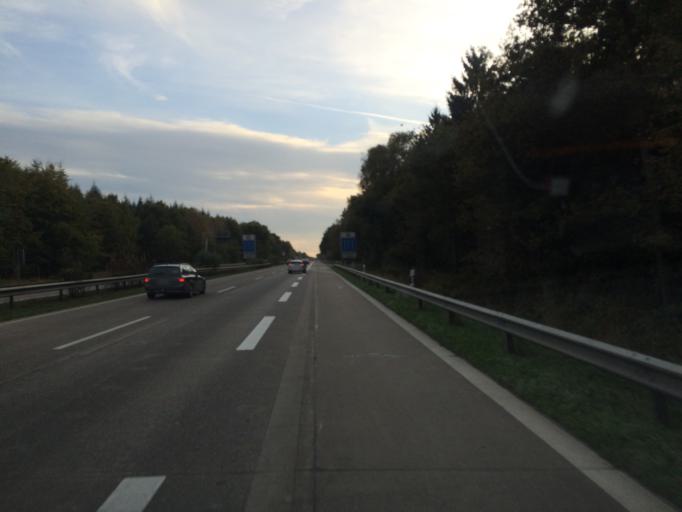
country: DE
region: Lower Saxony
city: Bad Fallingbostel
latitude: 52.8816
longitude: 9.7542
